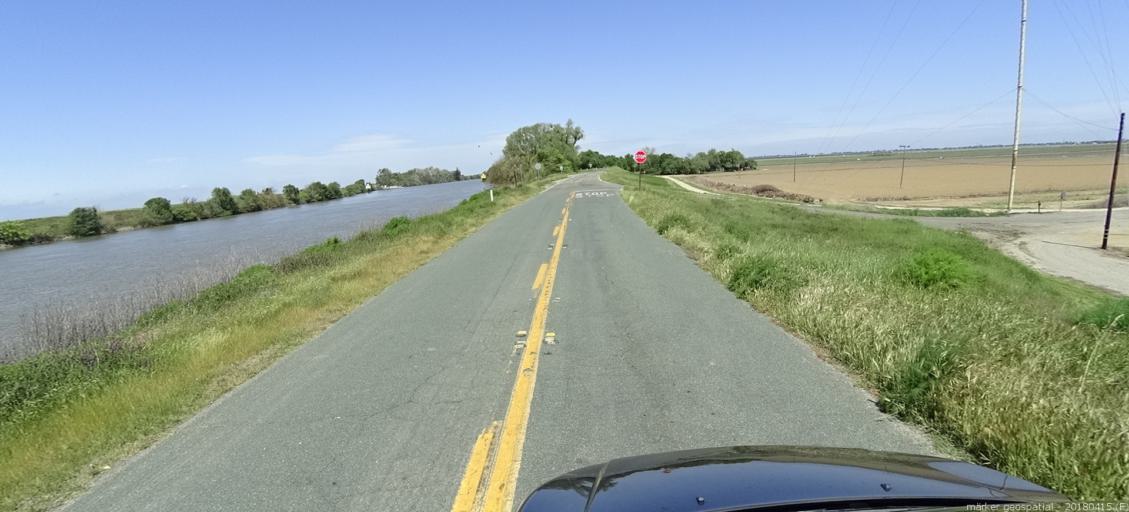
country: US
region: California
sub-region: Sacramento County
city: Walnut Grove
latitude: 38.2297
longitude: -121.6017
